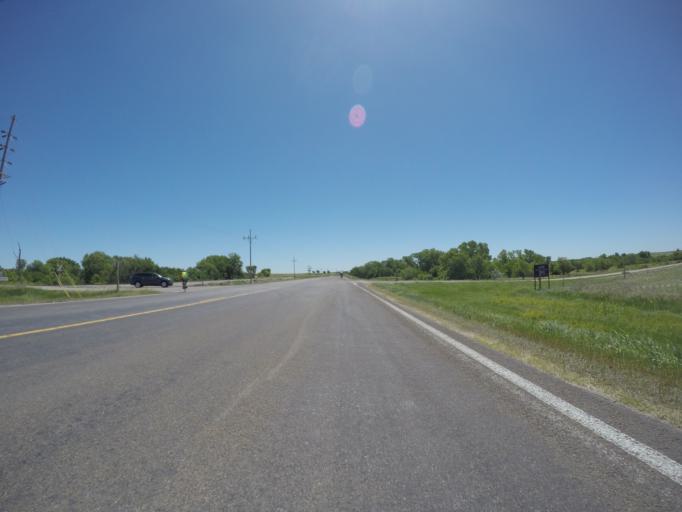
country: US
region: Kansas
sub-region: Phillips County
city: Phillipsburg
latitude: 39.8194
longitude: -99.5341
